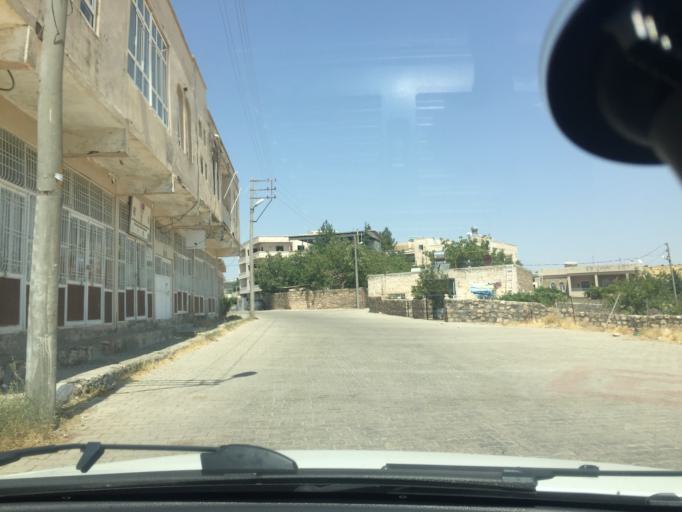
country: TR
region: Mardin
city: Kindirip
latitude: 37.4499
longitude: 41.2226
